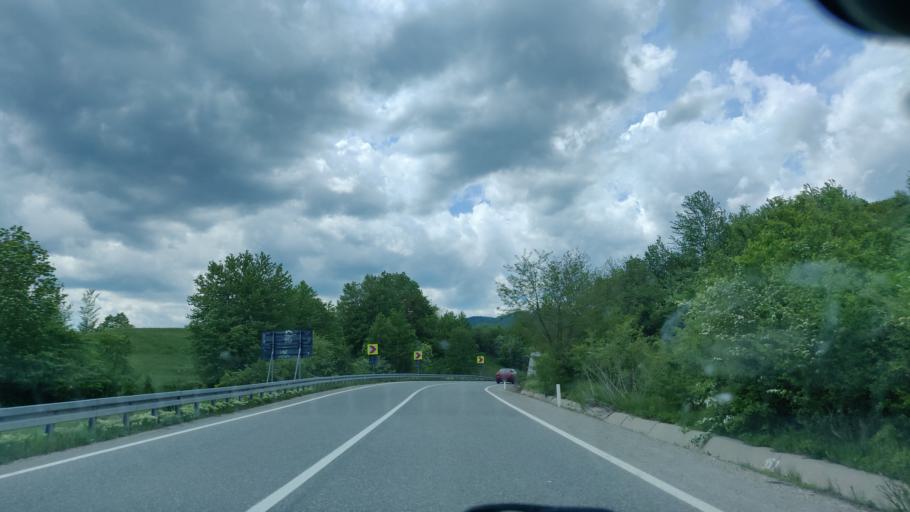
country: RO
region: Vrancea
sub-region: Comuna Negrilesti
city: Negrilesti
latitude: 45.9221
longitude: 26.7030
